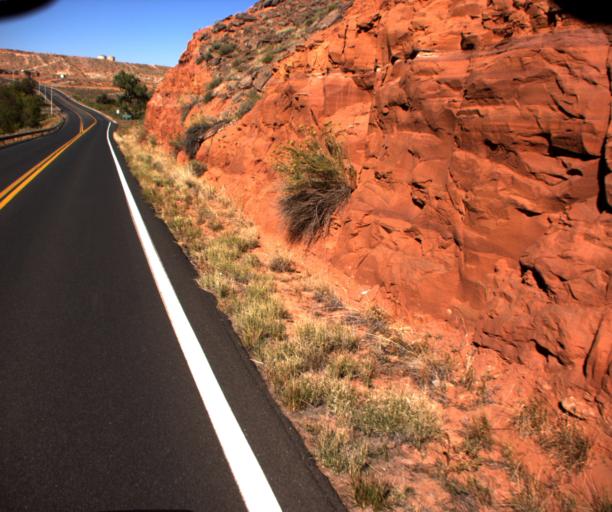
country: US
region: Arizona
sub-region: Coconino County
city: Tuba City
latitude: 36.1093
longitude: -111.2187
